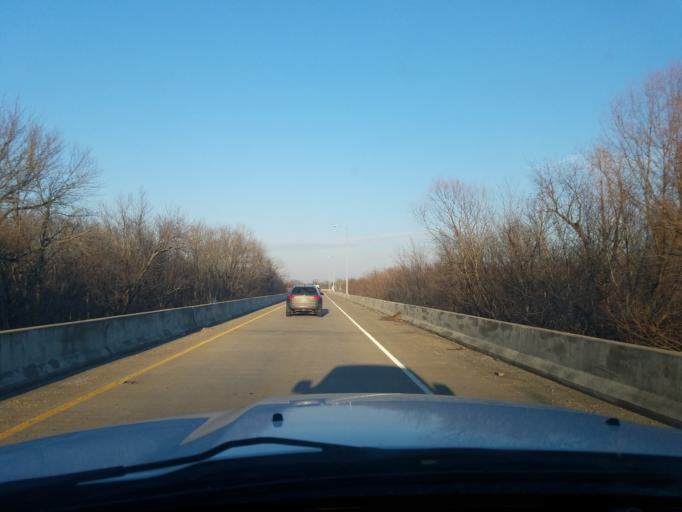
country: US
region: Indiana
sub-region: Vanderburgh County
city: Evansville
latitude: 37.9361
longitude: -87.5452
